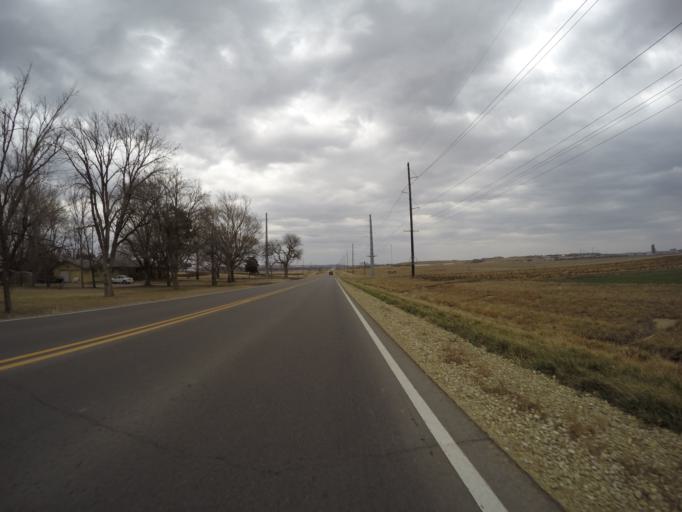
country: US
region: Kansas
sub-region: Riley County
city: Manhattan
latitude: 39.2185
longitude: -96.5995
